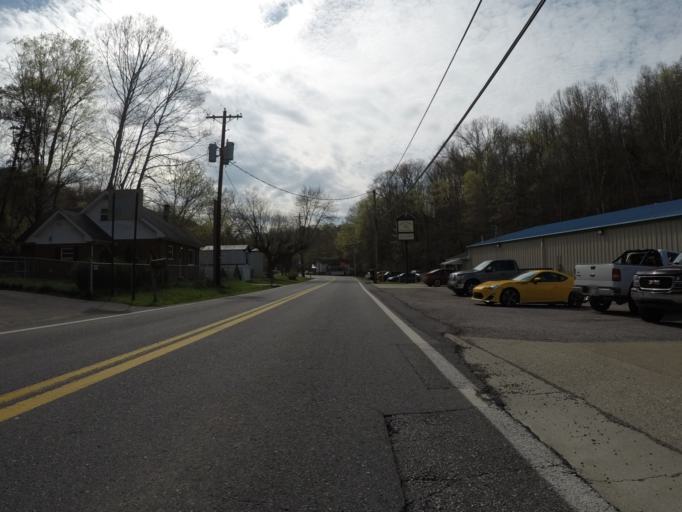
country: US
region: West Virginia
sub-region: Cabell County
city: Pea Ridge
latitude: 38.3771
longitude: -82.3728
